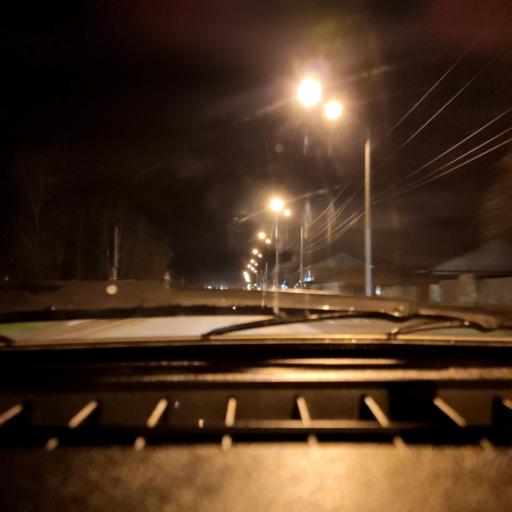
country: RU
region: Bashkortostan
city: Iglino
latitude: 54.7632
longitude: 56.2401
